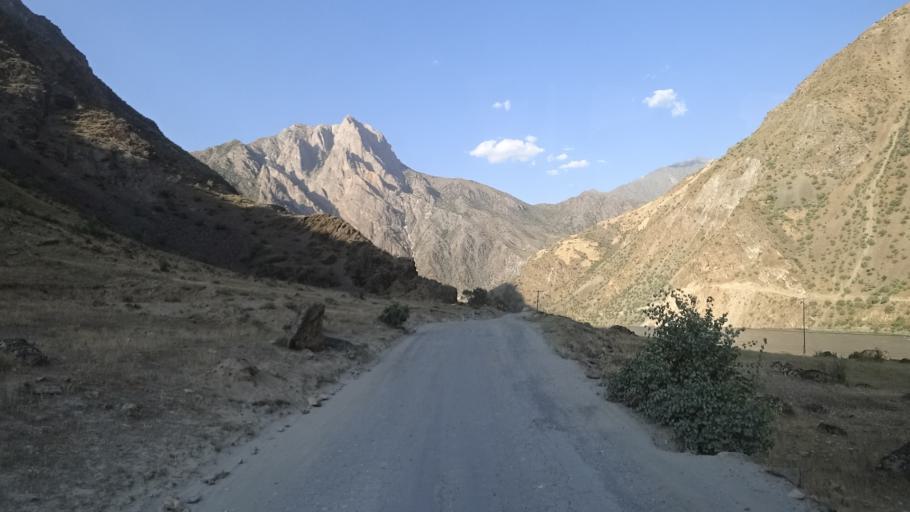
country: AF
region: Badakhshan
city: Maymay
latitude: 38.4801
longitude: 70.9746
